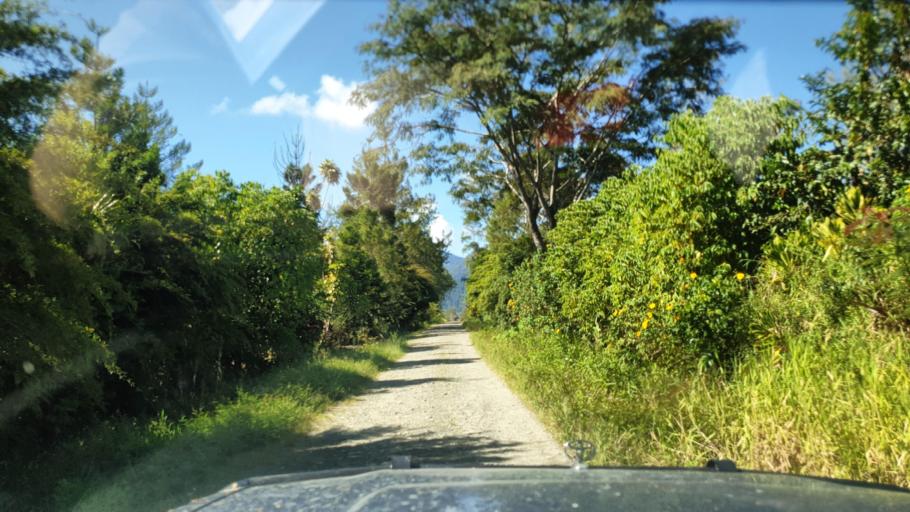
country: PG
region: Western Highlands
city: Rauna
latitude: -5.8090
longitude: 144.3768
